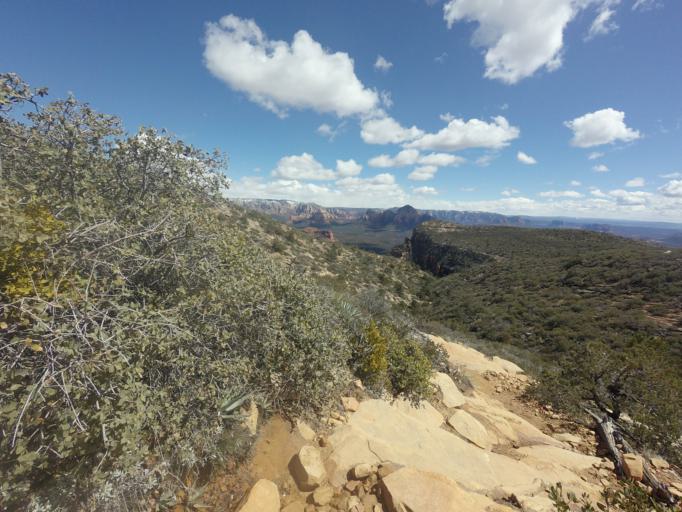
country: US
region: Arizona
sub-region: Yavapai County
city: West Sedona
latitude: 34.9100
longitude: -111.8764
